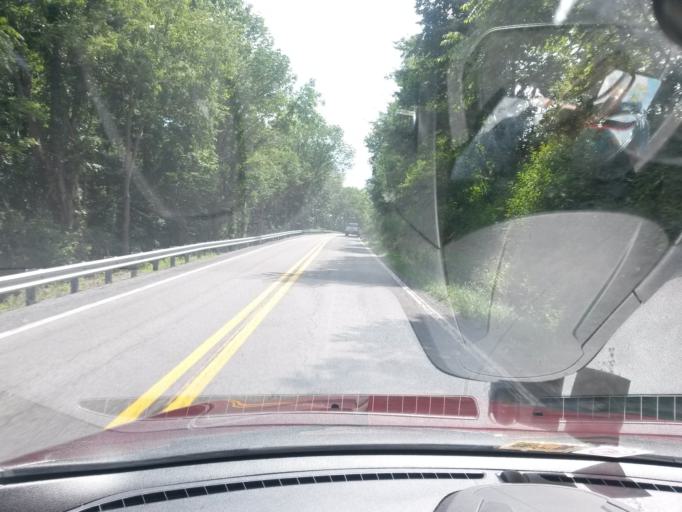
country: US
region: West Virginia
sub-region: Pendleton County
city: Franklin
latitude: 38.5692
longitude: -79.4209
